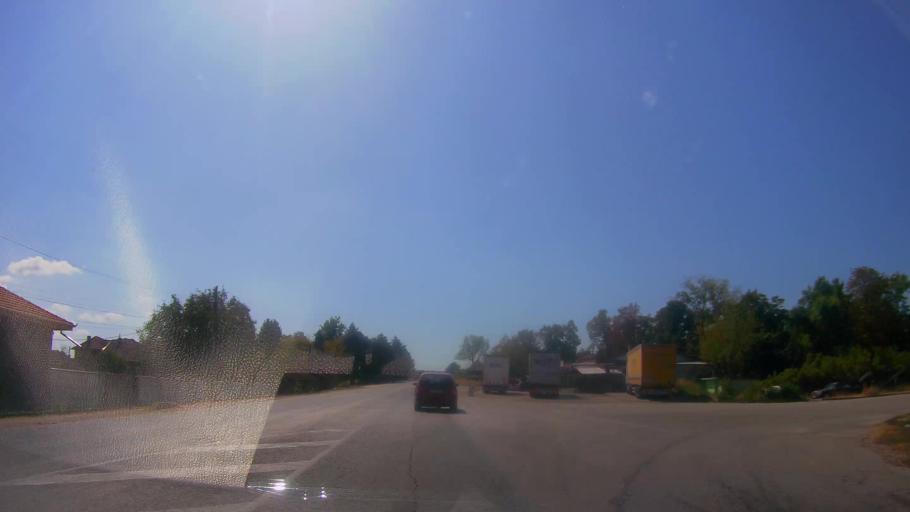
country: BG
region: Veliko Turnovo
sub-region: Obshtina Gorna Oryakhovitsa
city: Purvomaytsi
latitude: 43.2665
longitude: 25.6435
